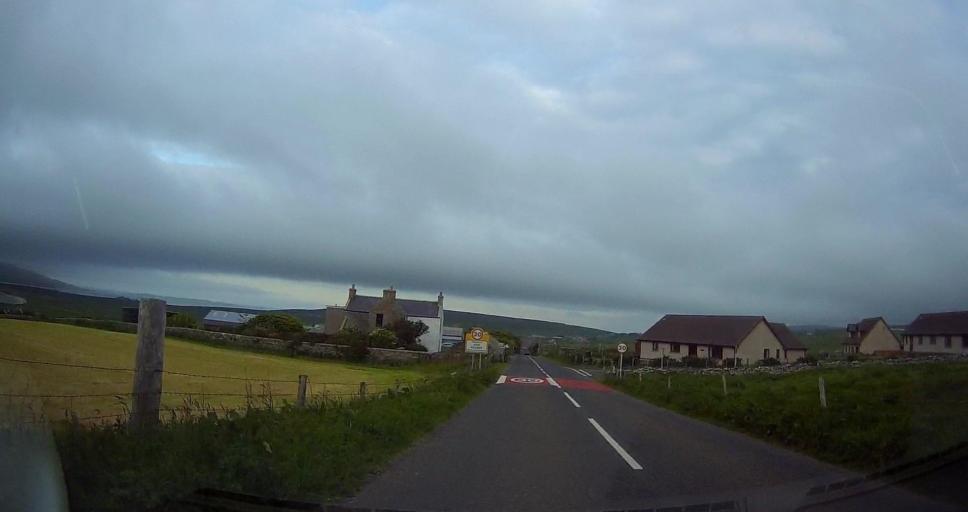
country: GB
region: Scotland
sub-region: Orkney Islands
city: Orkney
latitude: 59.1145
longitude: -3.1126
